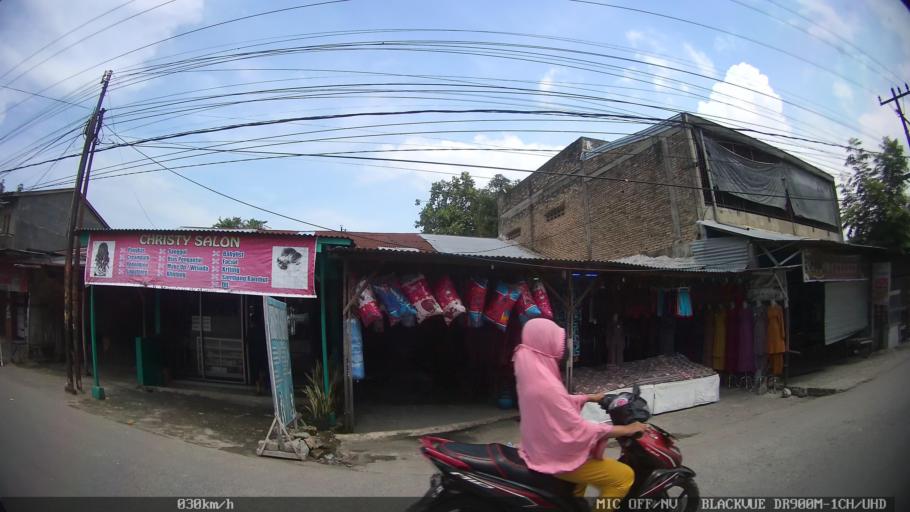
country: ID
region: North Sumatra
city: Labuhan Deli
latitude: 3.6614
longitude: 98.6781
